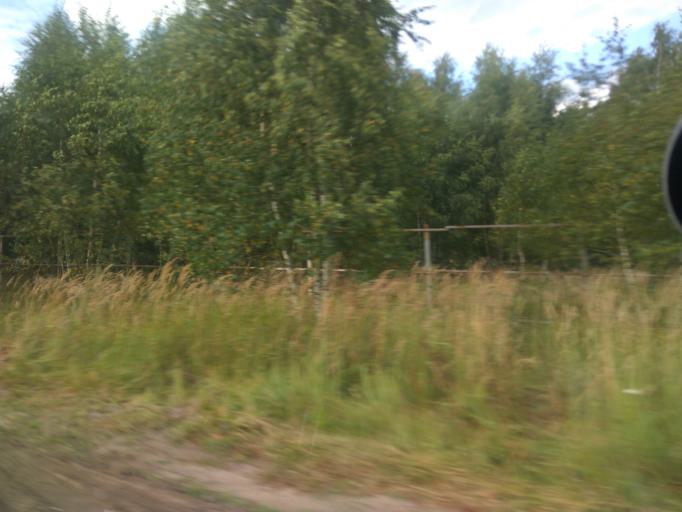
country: RU
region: Moskovskaya
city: Bronnitsy
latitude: 55.4671
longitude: 38.2794
